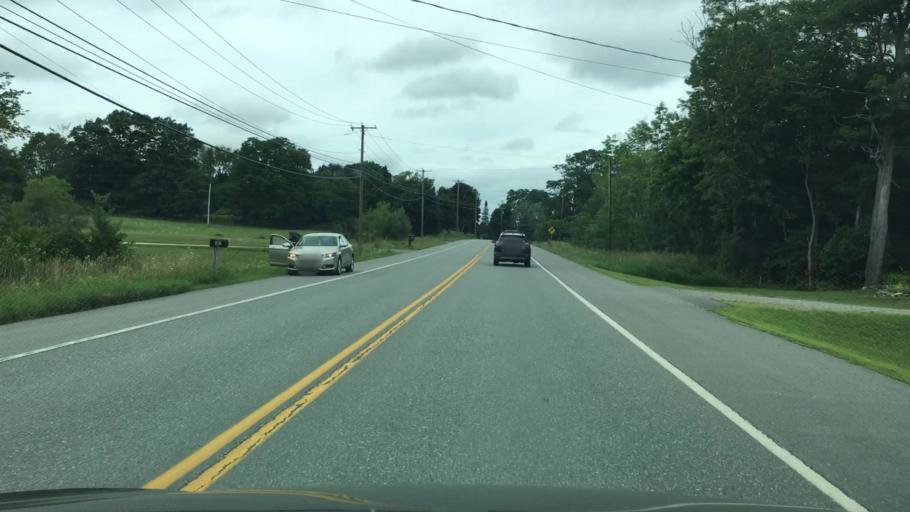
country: US
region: Maine
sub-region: Penobscot County
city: Orrington
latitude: 44.7128
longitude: -68.8265
